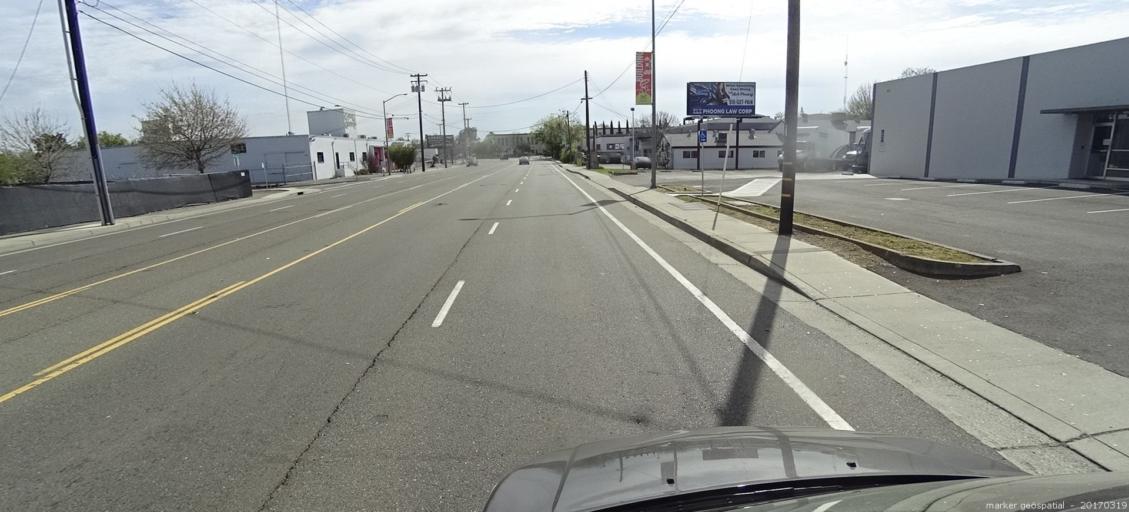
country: US
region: California
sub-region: Sacramento County
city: Sacramento
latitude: 38.5955
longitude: -121.4898
